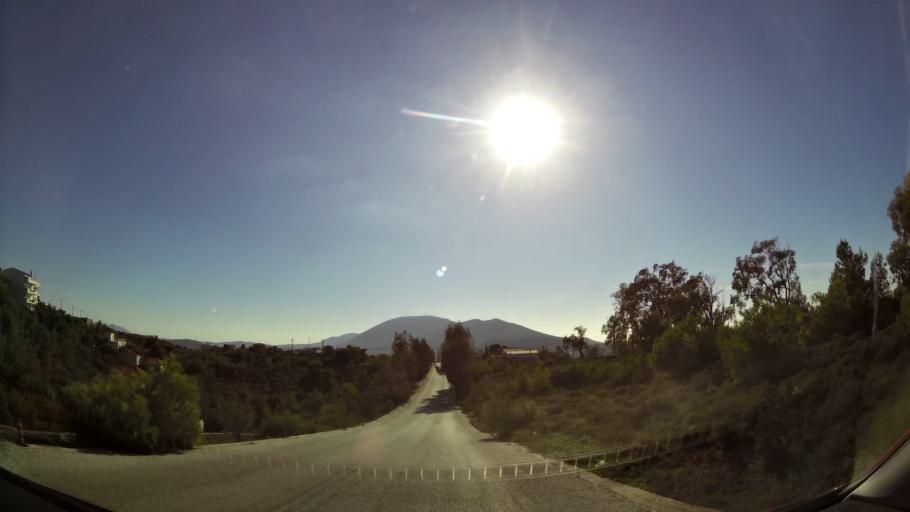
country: GR
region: Attica
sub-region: Nomarchia Anatolikis Attikis
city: Anthousa
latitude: 38.0304
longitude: 23.8715
